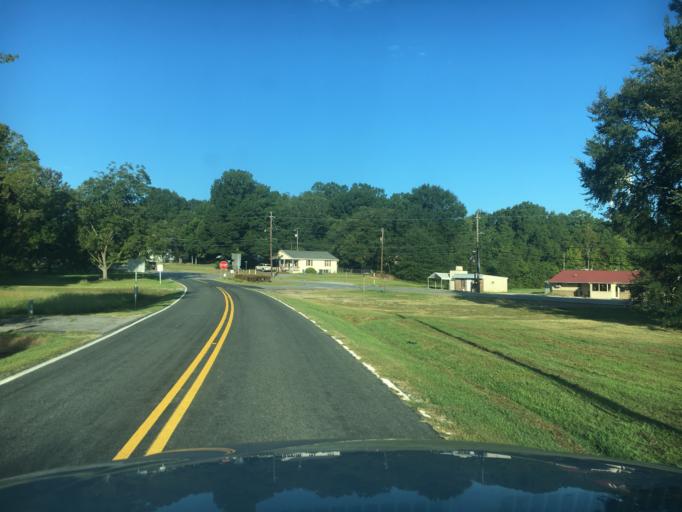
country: US
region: South Carolina
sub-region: Greenville County
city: Fountain Inn
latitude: 34.6088
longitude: -82.1098
